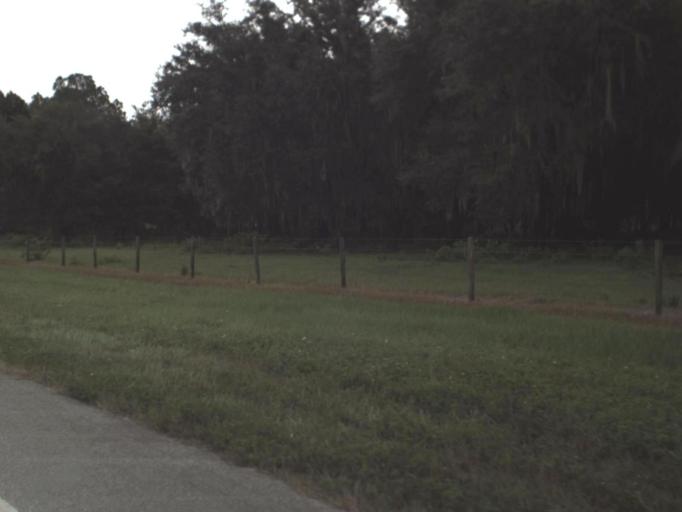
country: US
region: Florida
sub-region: Hillsborough County
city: Balm
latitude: 27.5897
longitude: -82.0910
